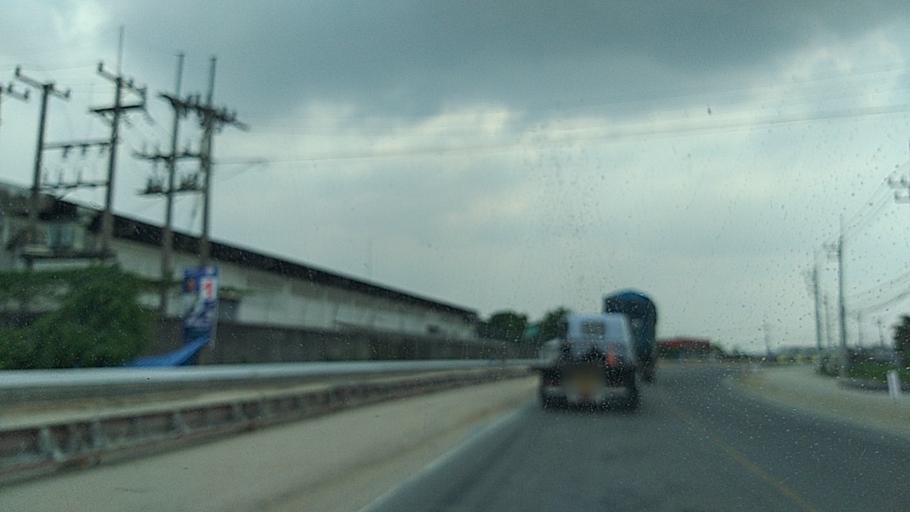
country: TH
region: Chon Buri
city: Ban Bueng
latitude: 13.3136
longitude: 101.1840
